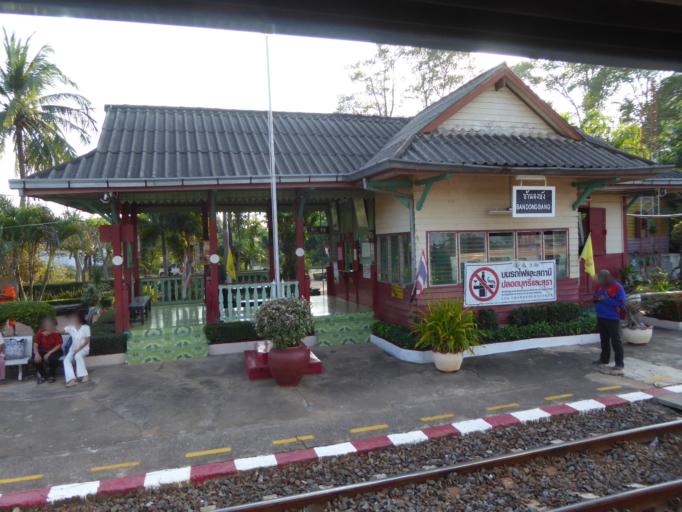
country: TH
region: Prachin Buri
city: Prachantakham
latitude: 14.0405
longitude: 101.5989
